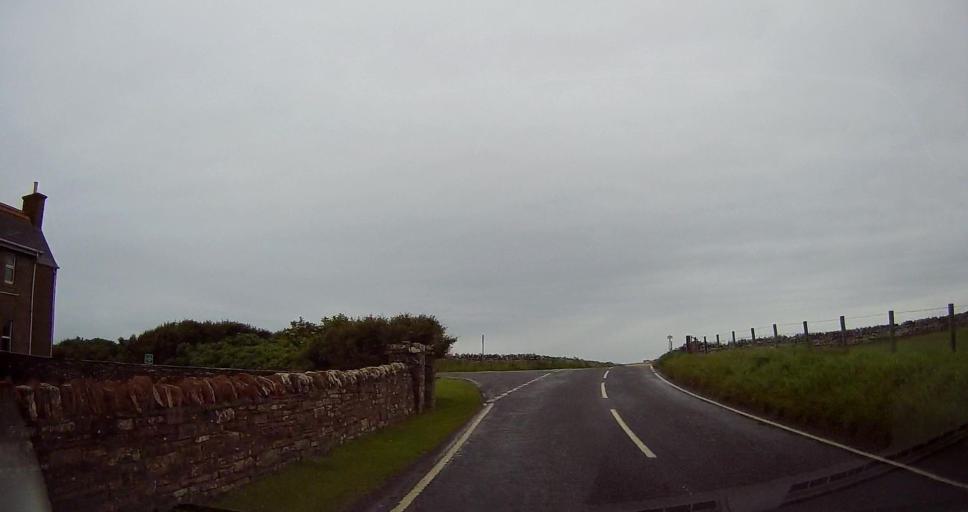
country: GB
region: Scotland
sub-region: Orkney Islands
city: Stromness
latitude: 59.1203
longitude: -3.3060
